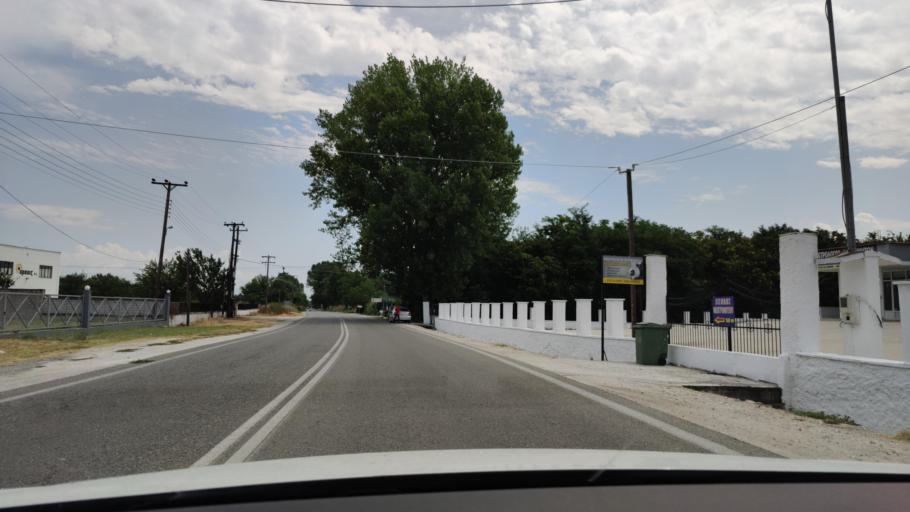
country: GR
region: Central Macedonia
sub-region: Nomos Serron
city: Serres
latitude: 41.0711
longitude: 23.5586
